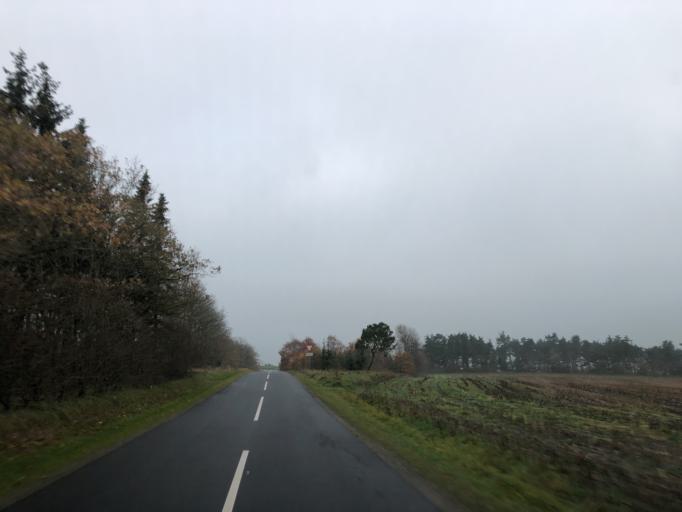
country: DK
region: Central Jutland
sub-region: Ringkobing-Skjern Kommune
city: Videbaek
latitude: 56.1880
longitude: 8.6427
